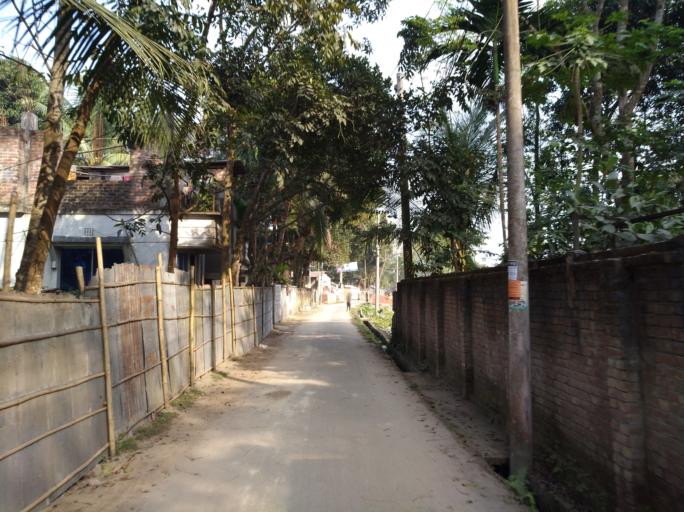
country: BD
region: Rajshahi
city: Saidpur
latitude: 25.9335
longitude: 88.8410
